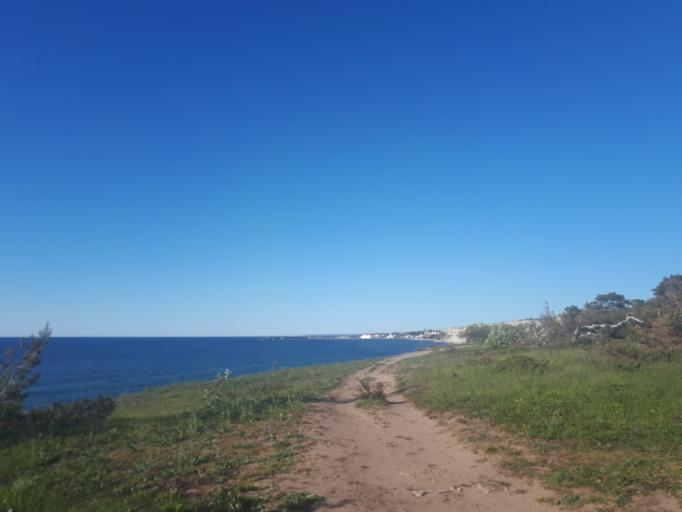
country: SE
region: Gotland
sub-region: Gotland
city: Vibble
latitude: 57.6146
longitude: 18.2521
